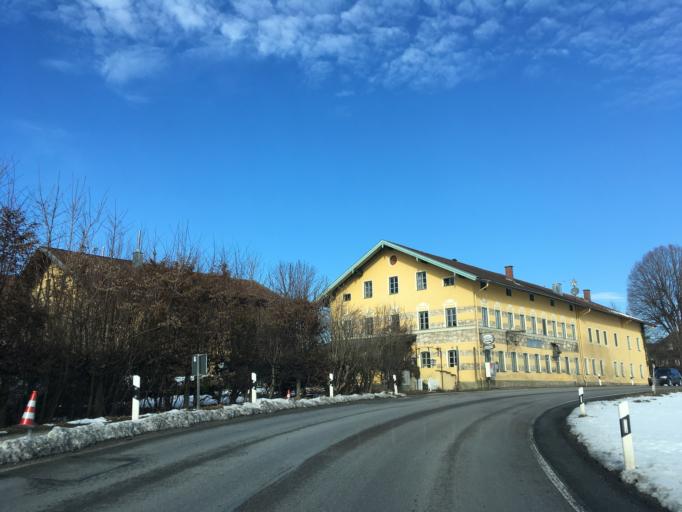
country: DE
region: Bavaria
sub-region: Upper Bavaria
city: Schechen
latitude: 47.8952
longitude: 12.1548
